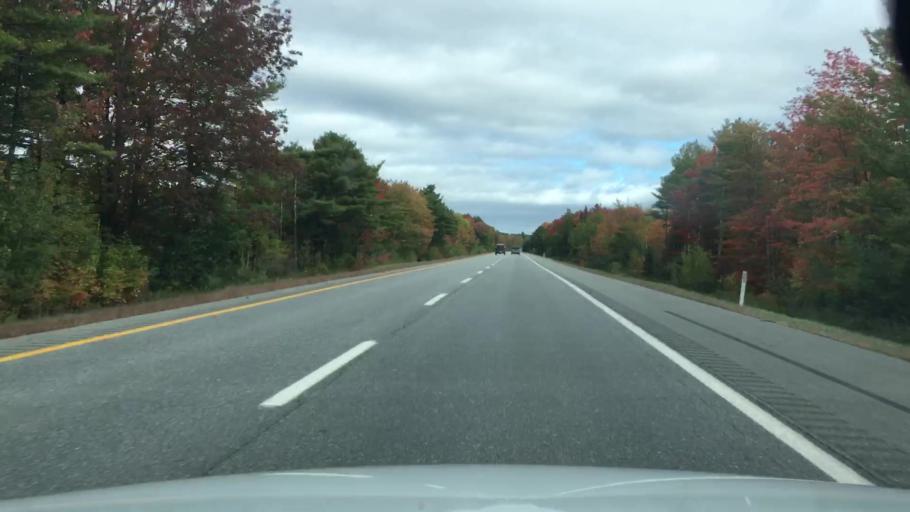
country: US
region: Maine
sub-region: Penobscot County
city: Carmel
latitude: 44.7737
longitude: -69.0292
